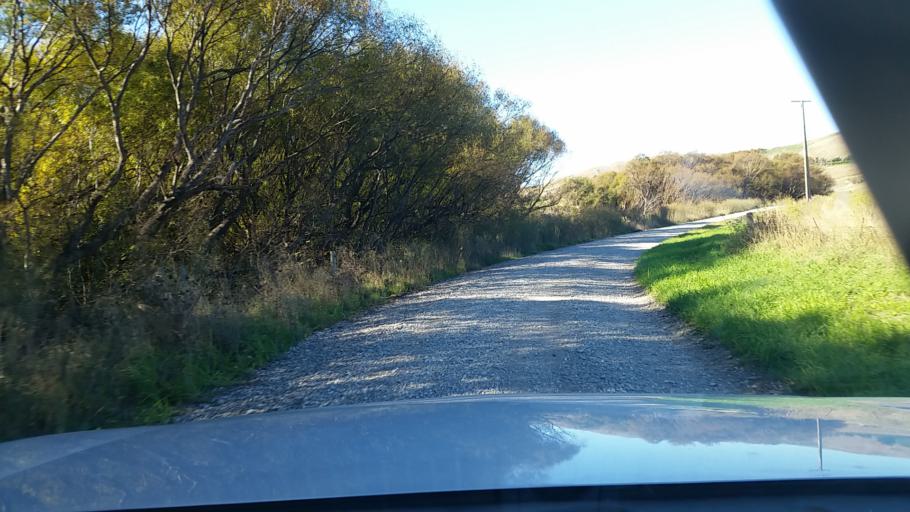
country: NZ
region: Marlborough
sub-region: Marlborough District
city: Blenheim
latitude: -41.6782
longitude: 174.1368
